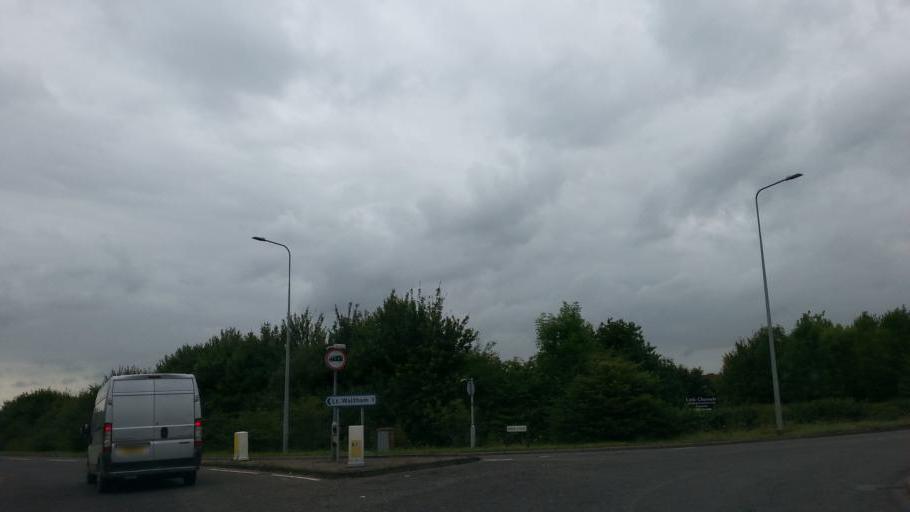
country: GB
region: England
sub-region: Essex
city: Chelmsford
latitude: 51.7773
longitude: 0.4879
